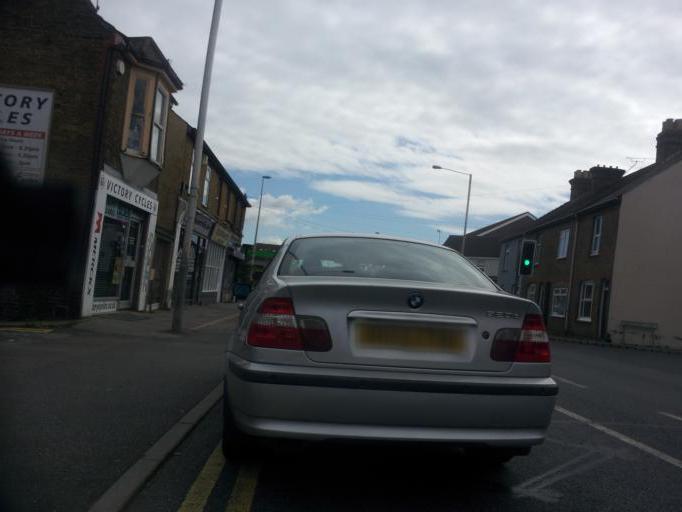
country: GB
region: England
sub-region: Kent
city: Rainham
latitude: 51.3621
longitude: 0.6143
